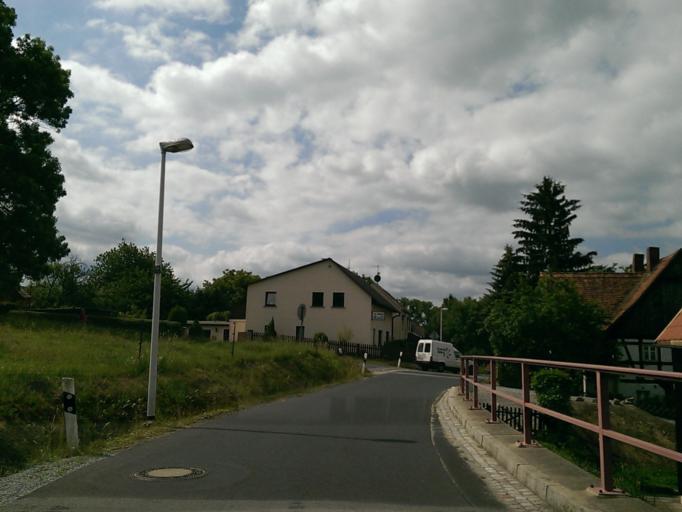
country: DE
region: Saxony
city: Mittelherwigsdorf
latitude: 50.9210
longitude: 14.7665
